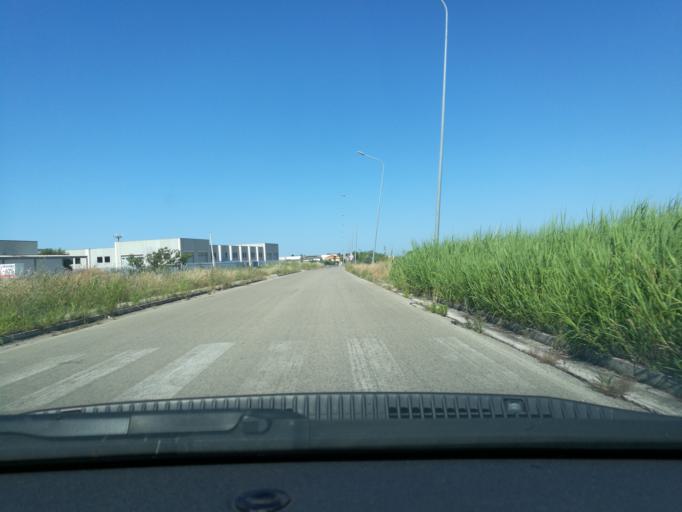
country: IT
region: Abruzzo
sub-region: Provincia di Chieti
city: Vasto
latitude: 42.1652
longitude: 14.6892
